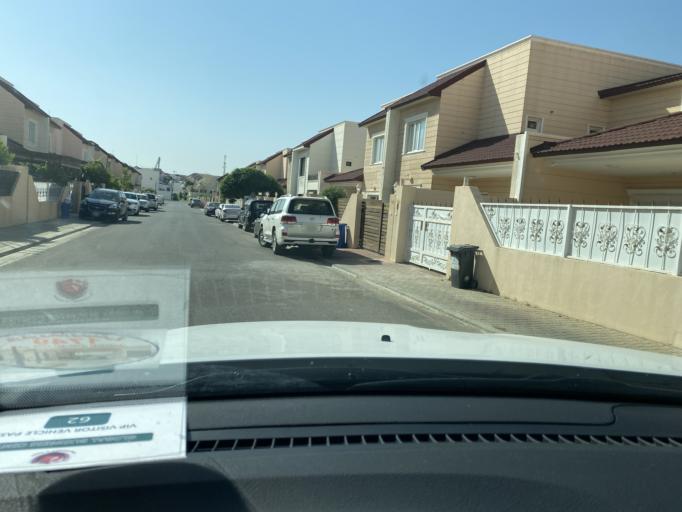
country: IQ
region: Arbil
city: Erbil
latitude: 36.2430
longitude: 44.0497
